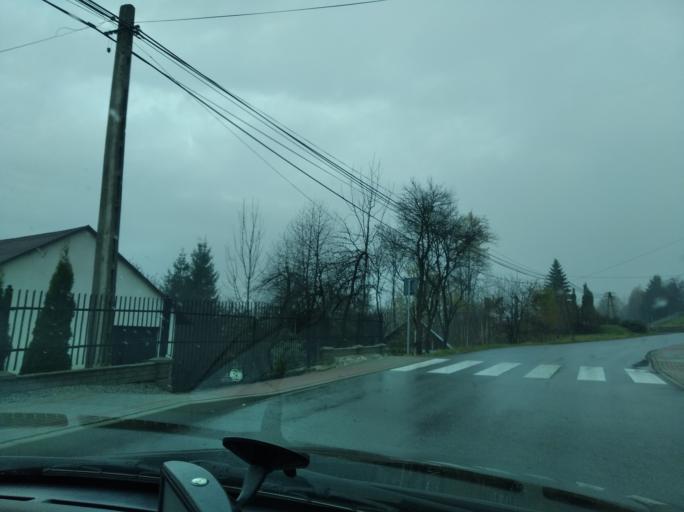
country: PL
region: Subcarpathian Voivodeship
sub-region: Powiat rzeszowski
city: Lubenia
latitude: 49.9293
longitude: 21.9272
